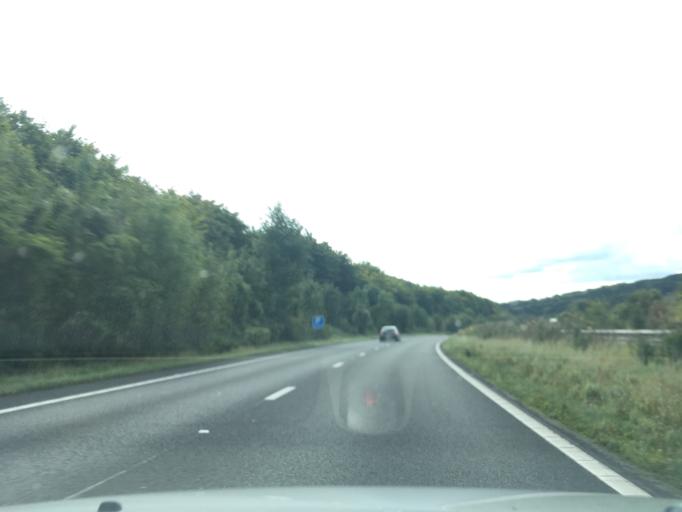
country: GB
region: England
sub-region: Hampshire
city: Petersfield
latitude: 50.9713
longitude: -0.9732
